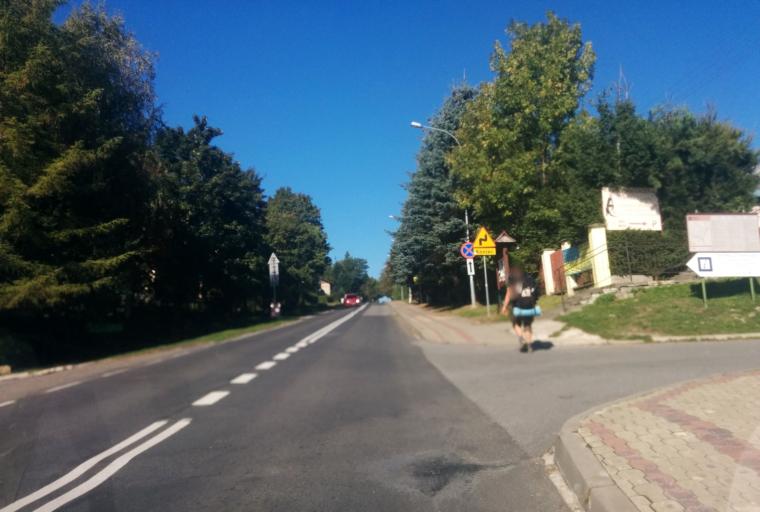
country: PL
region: Subcarpathian Voivodeship
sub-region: Powiat bieszczadzki
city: Lutowiska
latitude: 49.2512
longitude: 22.6954
